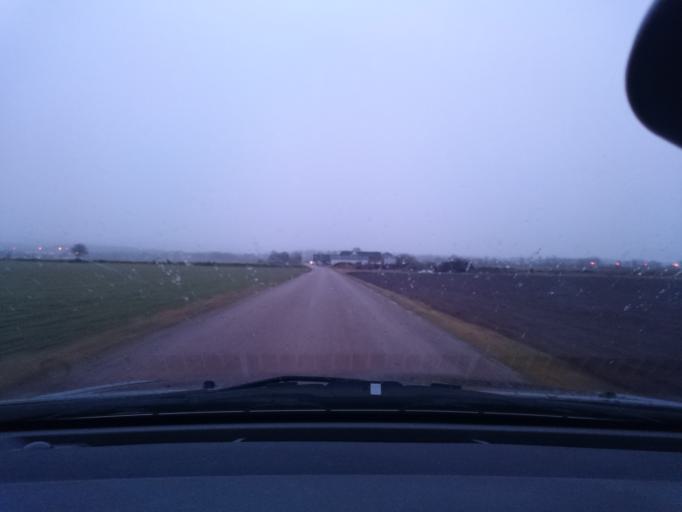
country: SE
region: Skane
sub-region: Bastads Kommun
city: Forslov
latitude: 56.3454
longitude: 12.7865
